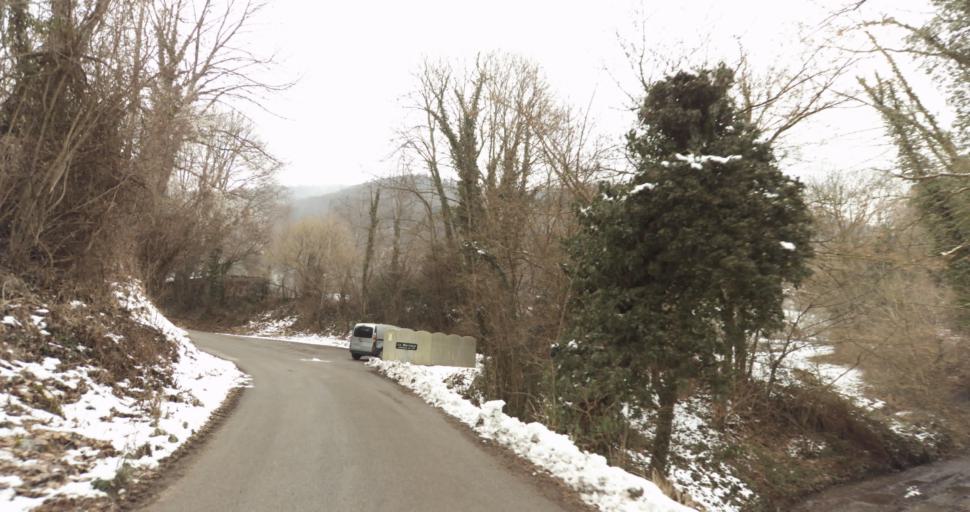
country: FR
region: Rhone-Alpes
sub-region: Departement de l'Isere
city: Vif
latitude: 45.0182
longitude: 5.6681
